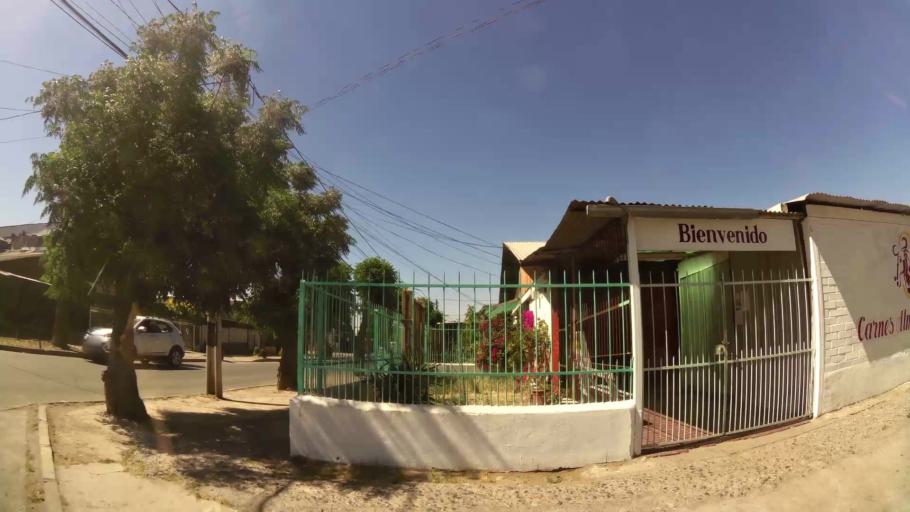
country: CL
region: Santiago Metropolitan
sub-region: Provincia de Maipo
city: San Bernardo
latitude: -33.5822
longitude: -70.6815
